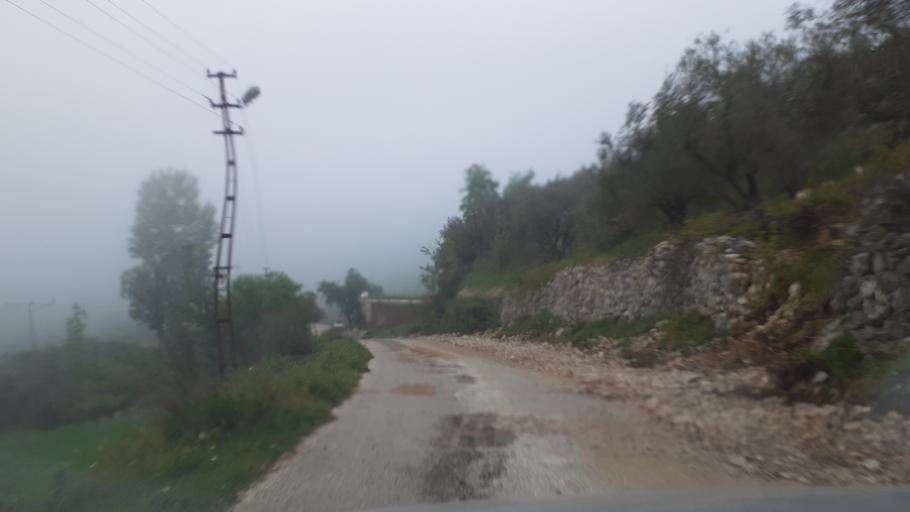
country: TR
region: Hatay
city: Yeditepe
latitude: 35.9707
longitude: 36.0038
